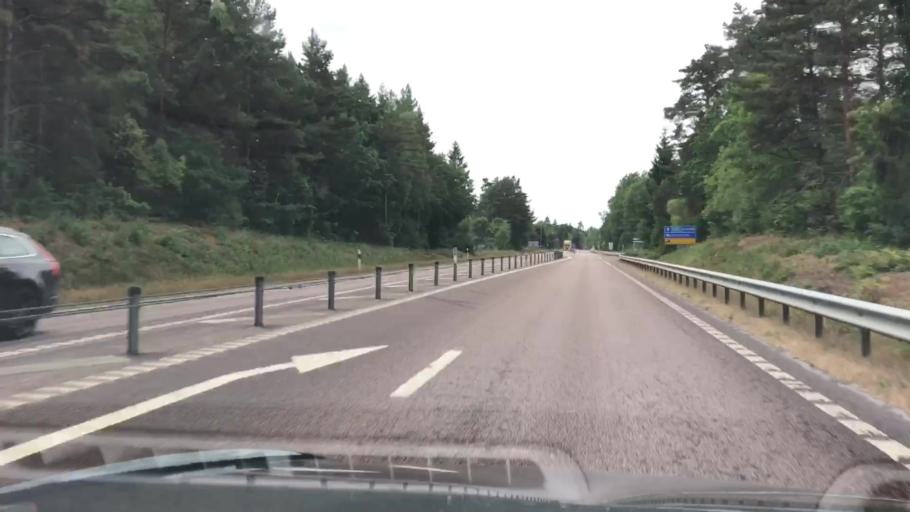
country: SE
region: Kalmar
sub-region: Torsas Kommun
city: Torsas
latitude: 56.2827
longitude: 15.9795
